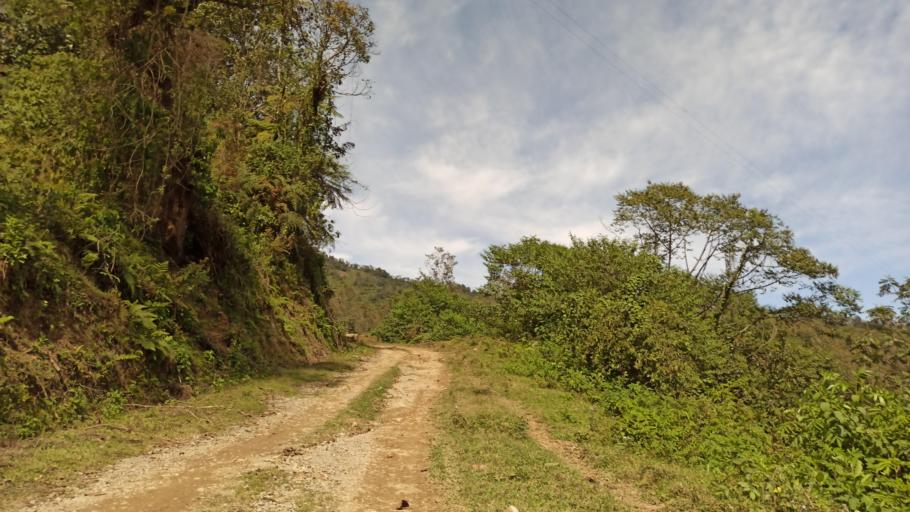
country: MX
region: Veracruz
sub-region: La Perla
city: Metlac Hernandez (Metlac Primero)
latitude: 18.9728
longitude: -97.1043
